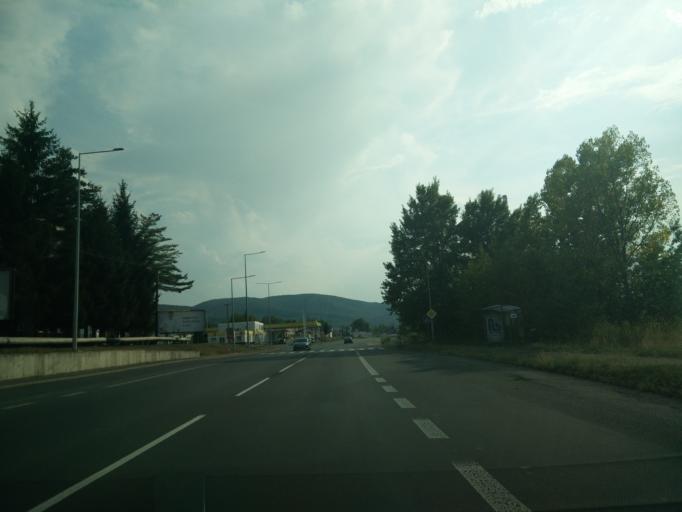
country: SK
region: Banskobystricky
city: Ziar nad Hronom
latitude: 48.5723
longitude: 18.8676
